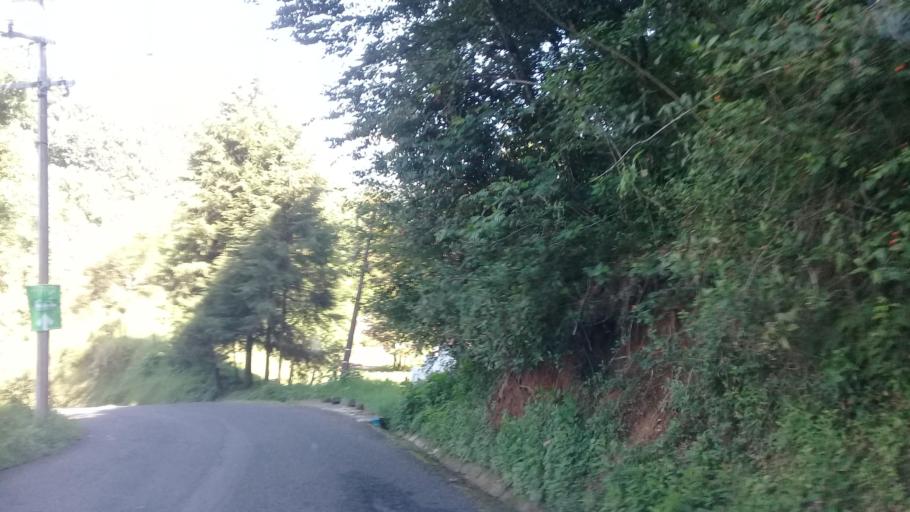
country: MX
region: Veracruz
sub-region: Tlalnelhuayocan
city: Guadalupe Victoria
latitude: 19.5293
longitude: -96.9502
